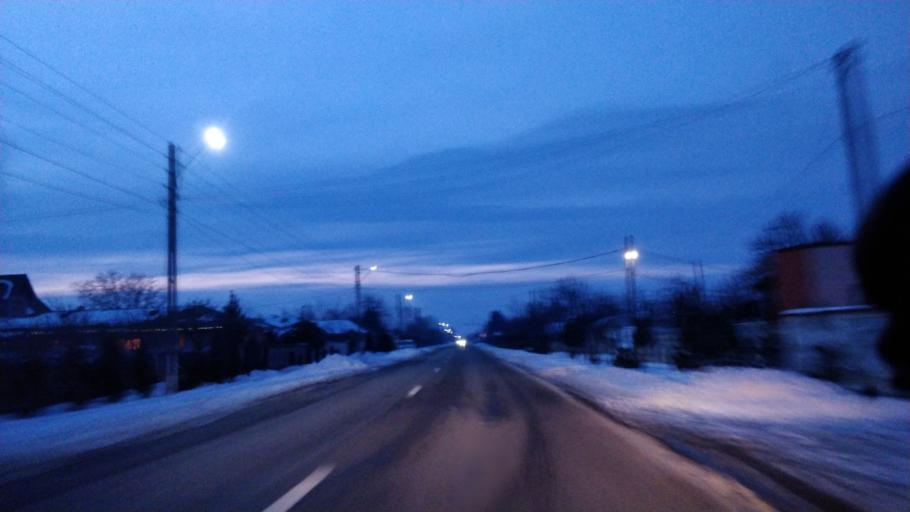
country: RO
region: Vrancea
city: Vulturu de Sus
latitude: 45.6138
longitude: 27.4347
